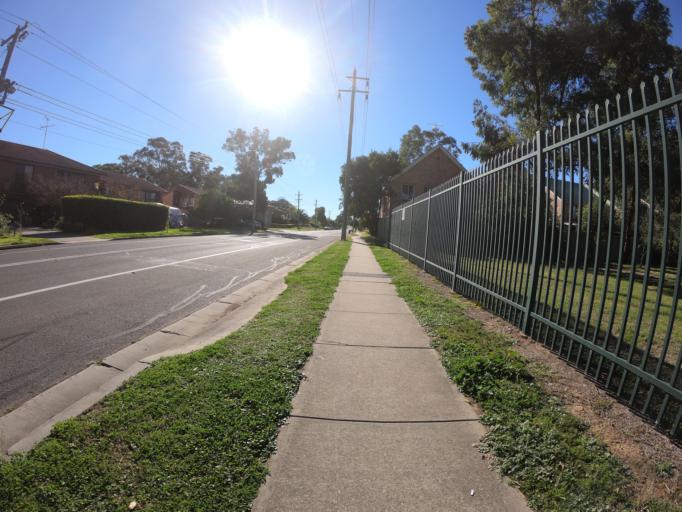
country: AU
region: New South Wales
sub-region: Hawkesbury
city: South Windsor
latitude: -33.6305
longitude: 150.7965
